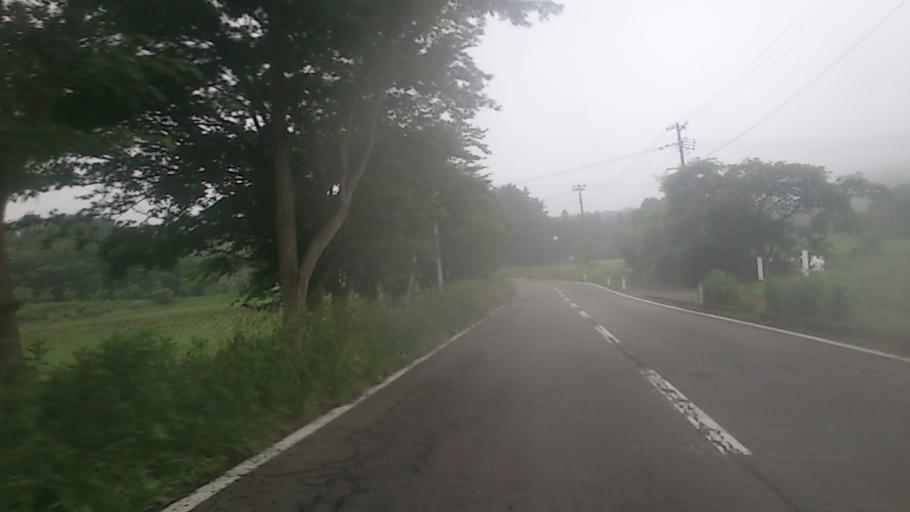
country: JP
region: Miyagi
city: Shiroishi
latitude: 38.0859
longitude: 140.5622
